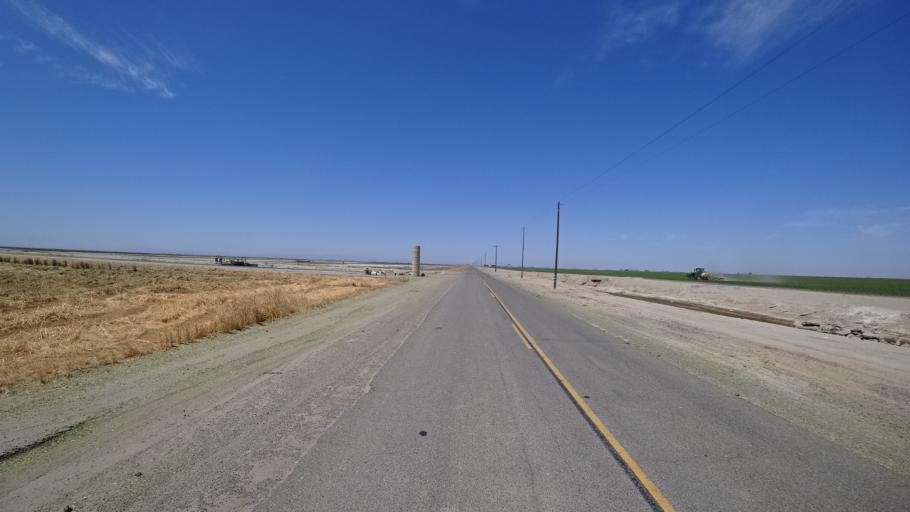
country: US
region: California
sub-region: Kings County
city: Corcoran
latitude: 36.1379
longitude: -119.6793
